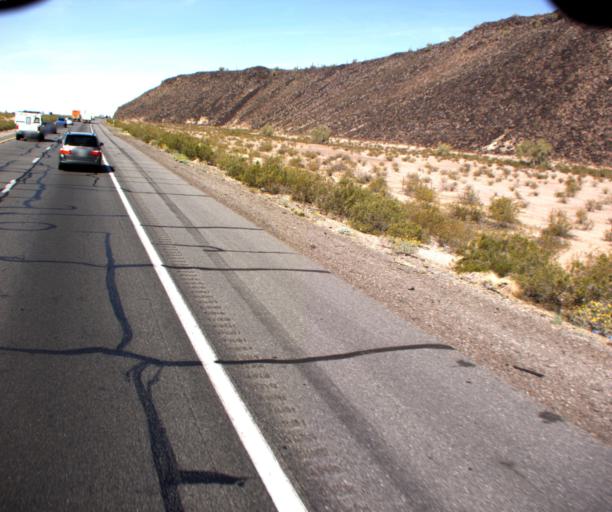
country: US
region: Arizona
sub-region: Maricopa County
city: Buckeye
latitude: 33.5272
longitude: -113.1070
